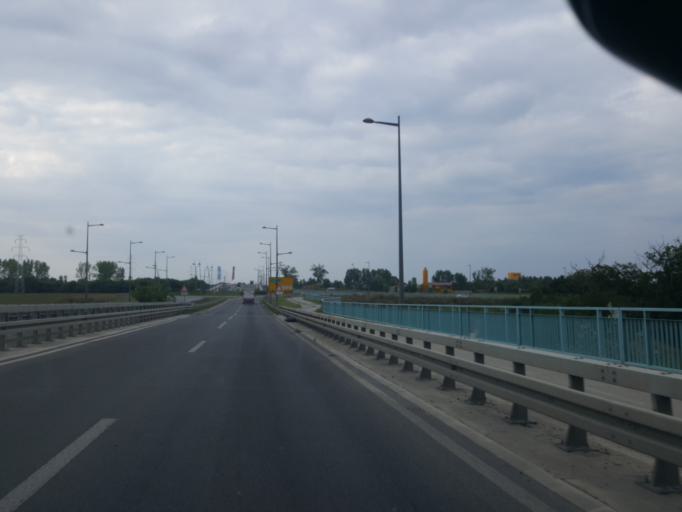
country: RS
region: Autonomna Pokrajina Vojvodina
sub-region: Juznobacki Okrug
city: Novi Sad
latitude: 45.2800
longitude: 19.8028
